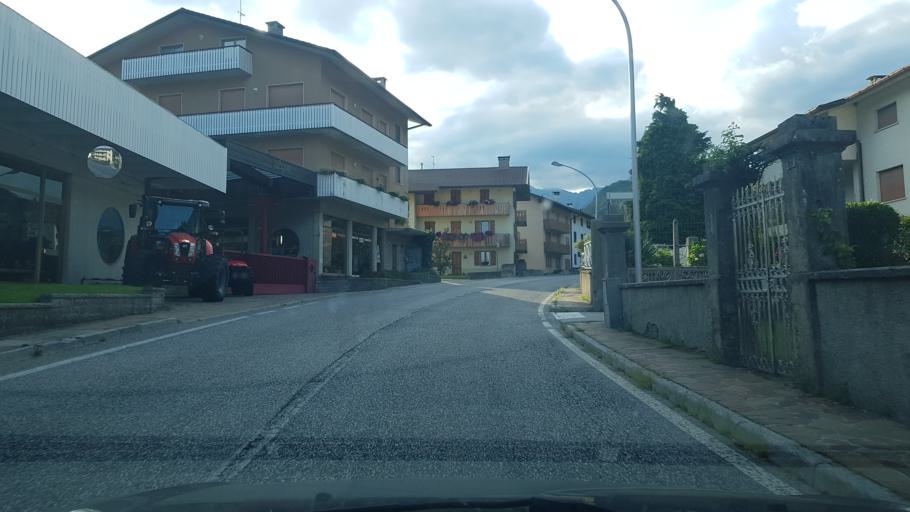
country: IT
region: Friuli Venezia Giulia
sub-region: Provincia di Udine
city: Villa Santina
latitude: 46.4183
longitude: 12.9139
